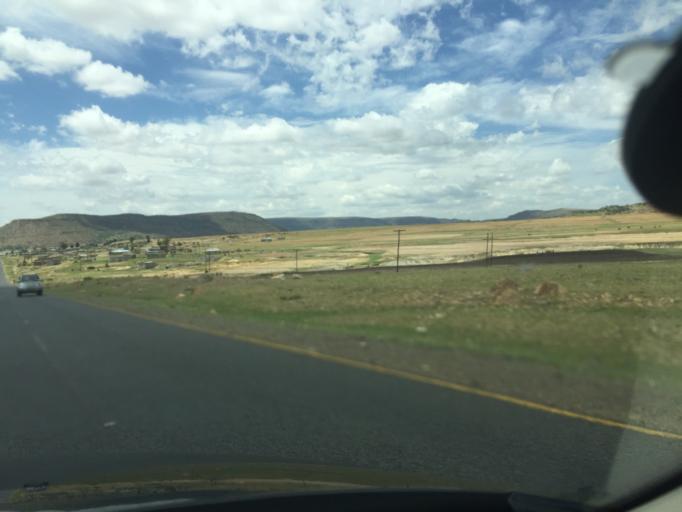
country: LS
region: Mafeteng
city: Mafeteng
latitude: -29.9335
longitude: 27.2612
